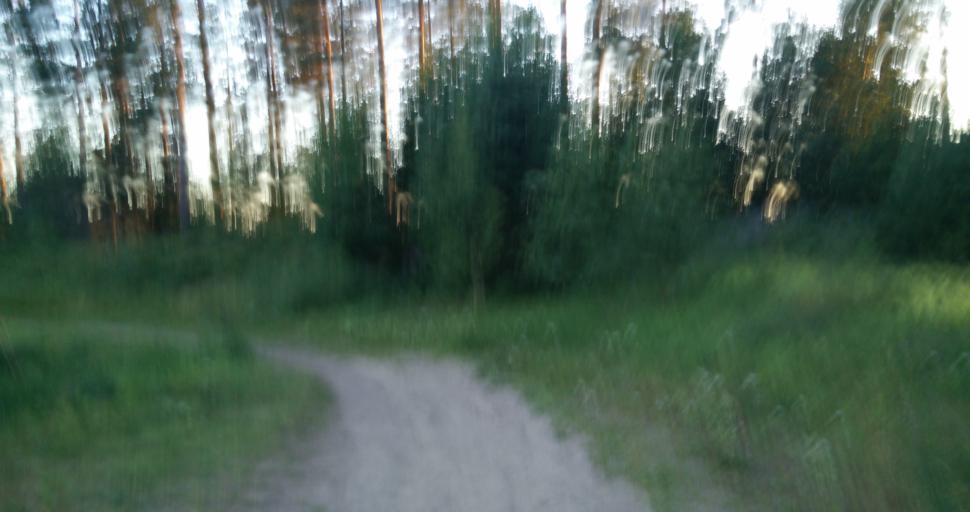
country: SE
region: Vaesternorrland
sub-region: Sundsvalls Kommun
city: Skottsund
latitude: 62.3136
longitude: 17.4047
